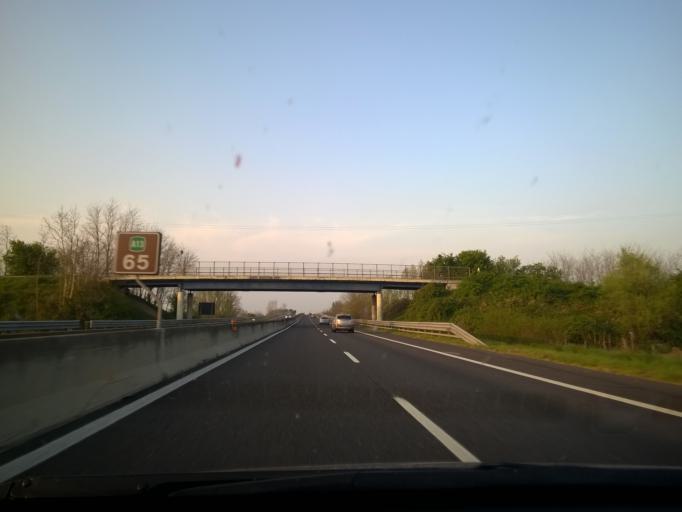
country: IT
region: Veneto
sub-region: Provincia di Rovigo
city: Costa di Rovigo
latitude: 45.0479
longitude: 11.7151
